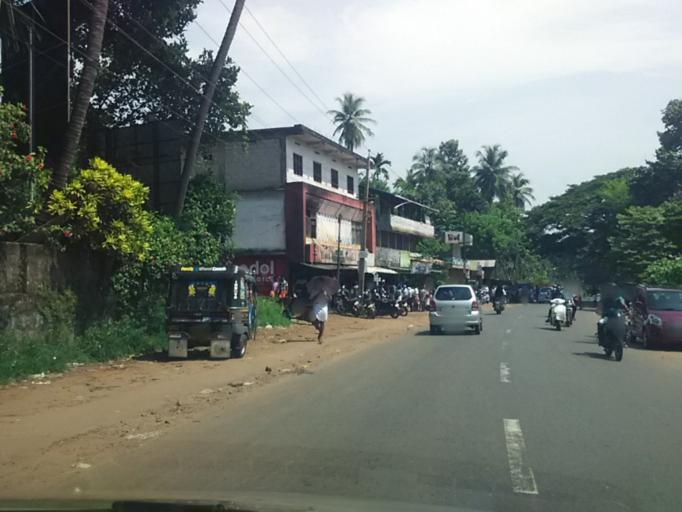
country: IN
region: Kerala
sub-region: Kozhikode
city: Kunnamangalam
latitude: 11.3095
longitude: 75.8818
